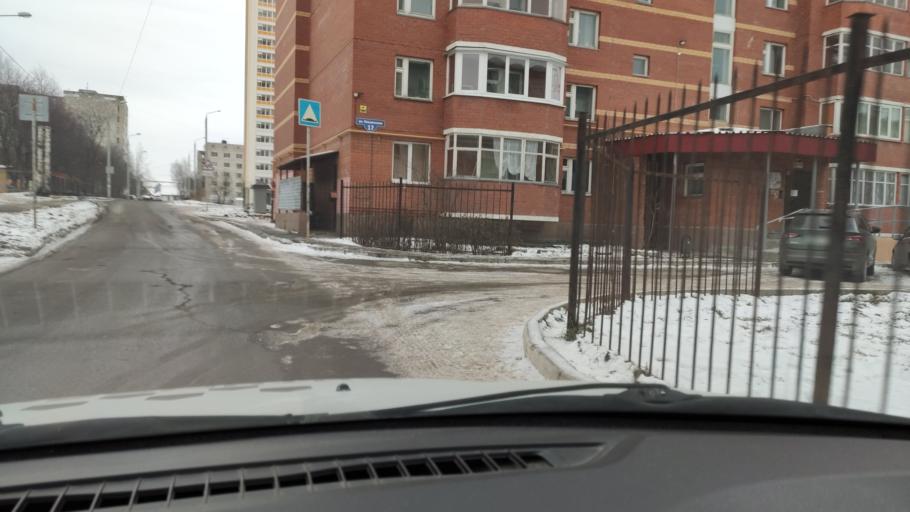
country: RU
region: Perm
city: Perm
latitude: 58.0646
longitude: 56.3592
